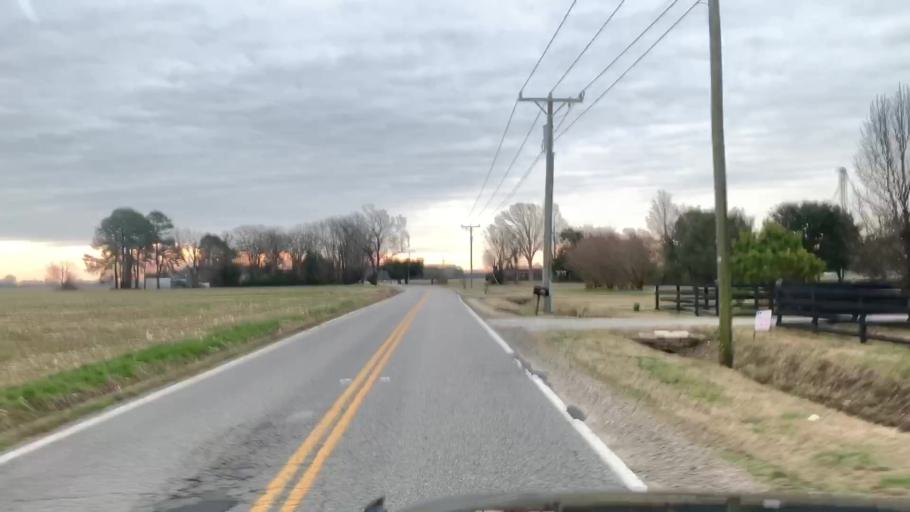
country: US
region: North Carolina
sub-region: Currituck County
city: Moyock
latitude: 36.6357
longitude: -76.1907
